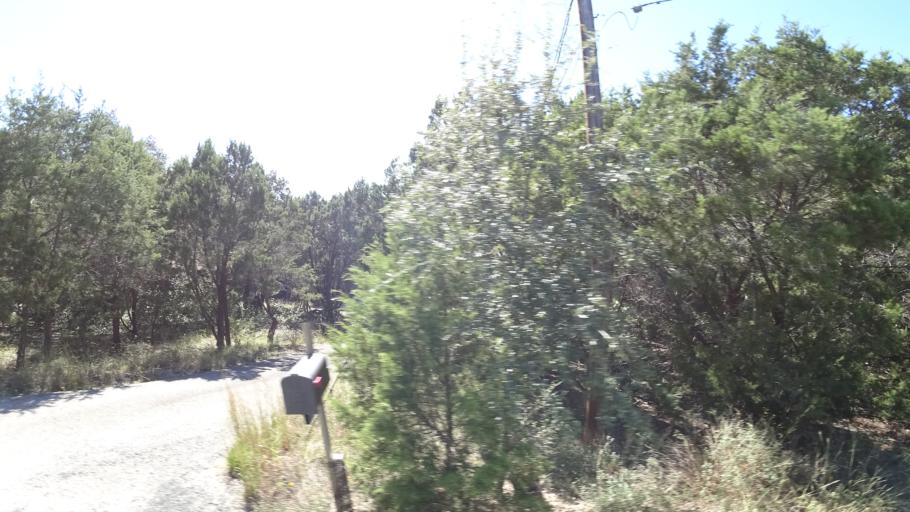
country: US
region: Texas
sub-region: Travis County
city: West Lake Hills
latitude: 30.3073
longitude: -97.8099
